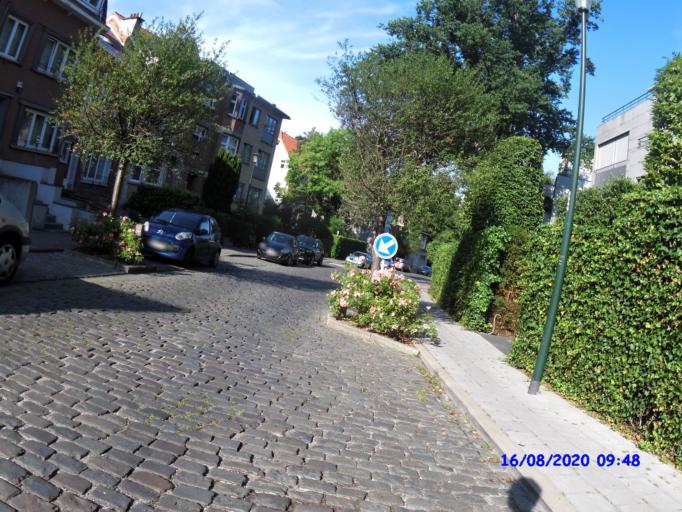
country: BE
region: Flanders
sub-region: Provincie Vlaams-Brabant
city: Drogenbos
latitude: 50.7959
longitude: 4.3406
